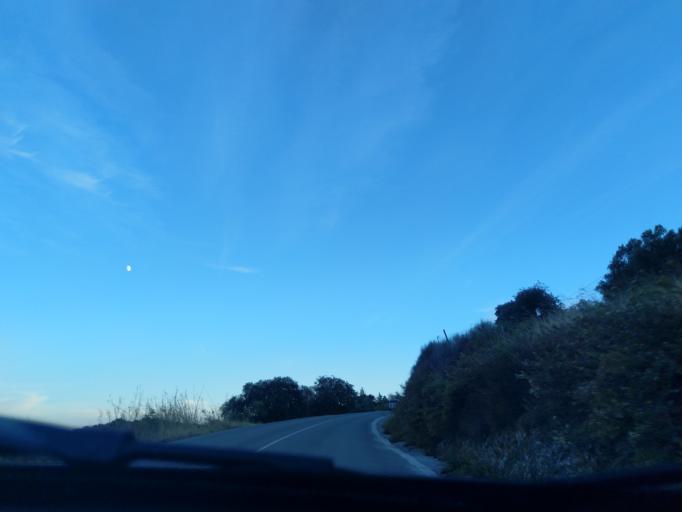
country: ES
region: Extremadura
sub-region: Provincia de Badajoz
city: Reina
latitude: 38.1585
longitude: -5.8983
